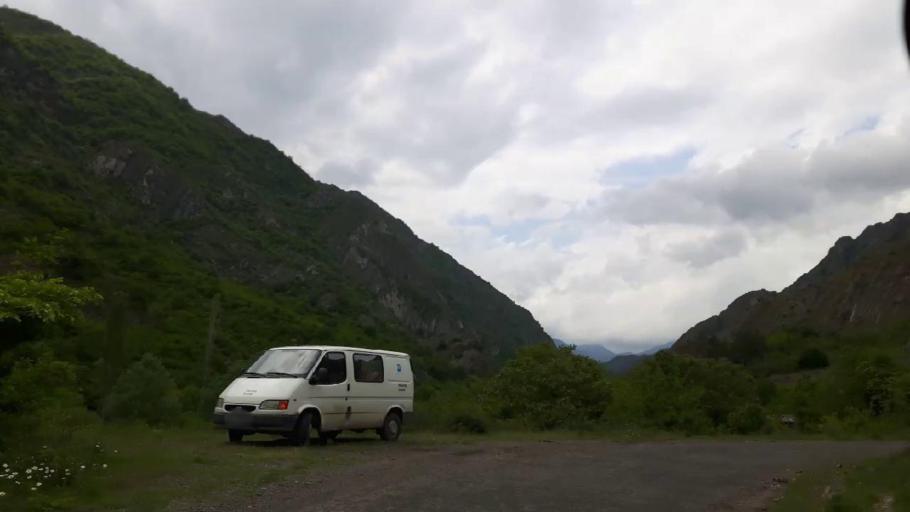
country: GE
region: Shida Kartli
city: Gori
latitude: 41.9004
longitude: 44.0852
